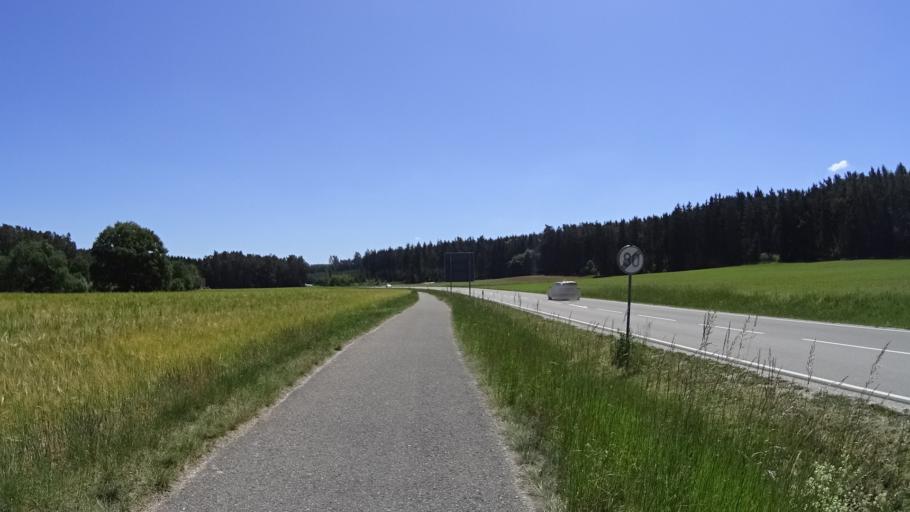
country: DE
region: Bavaria
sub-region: Regierungsbezirk Mittelfranken
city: Pleinfeld
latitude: 49.1005
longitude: 10.9574
